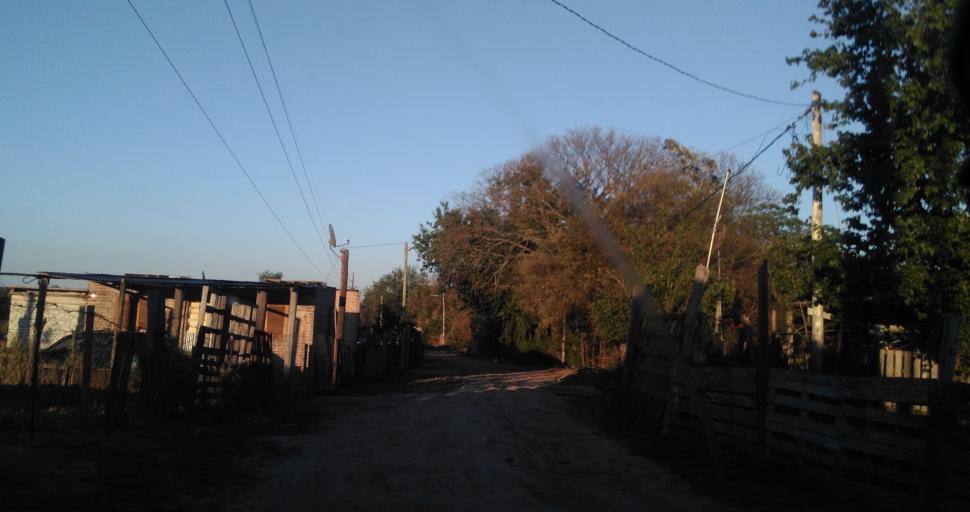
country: AR
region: Chaco
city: Fontana
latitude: -27.4249
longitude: -59.0164
